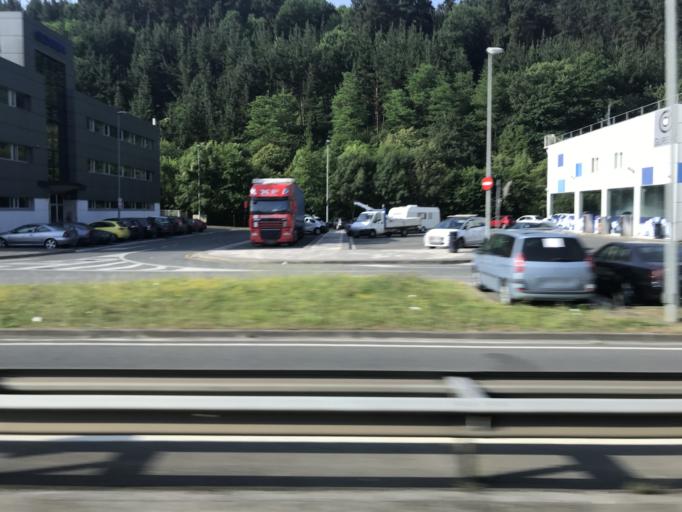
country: ES
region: Basque Country
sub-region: Provincia de Guipuzcoa
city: Beasain
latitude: 43.0451
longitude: -2.2020
